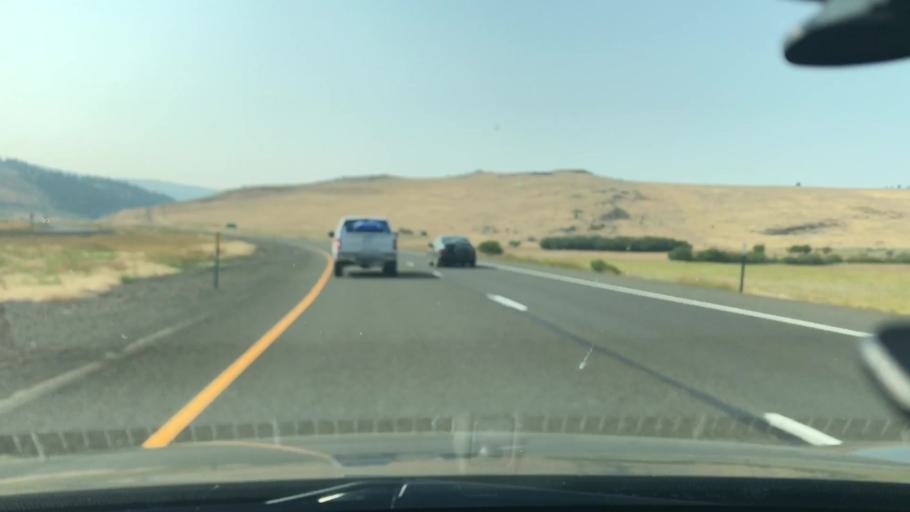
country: US
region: Oregon
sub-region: Union County
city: Union
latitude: 45.1694
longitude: -117.9668
